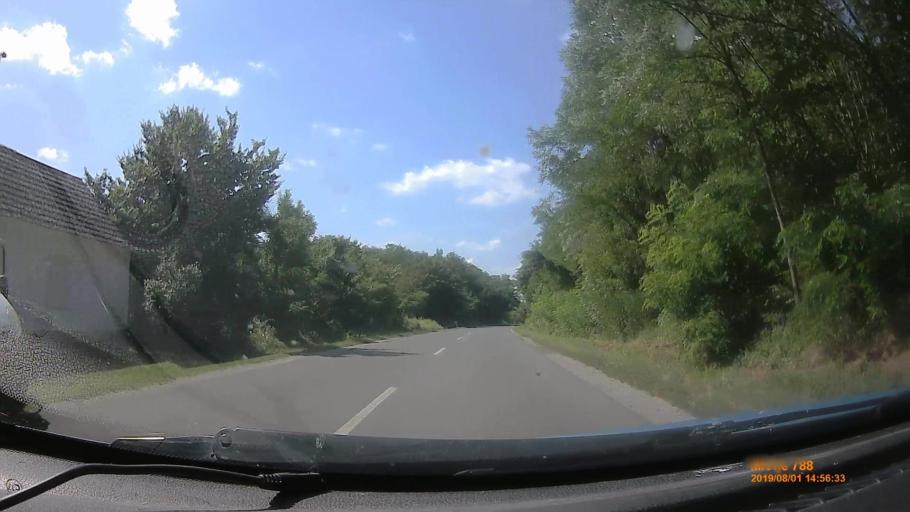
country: HU
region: Baranya
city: Vajszlo
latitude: 45.8773
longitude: 17.9433
